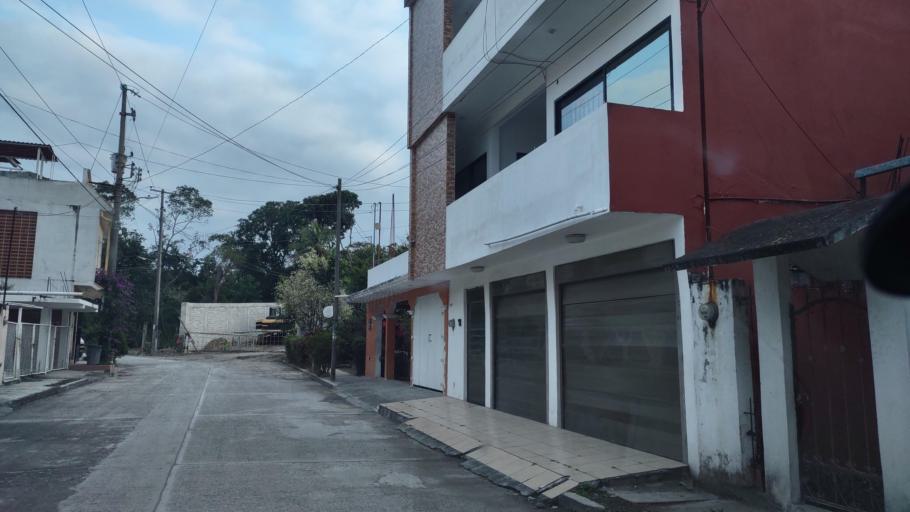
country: MX
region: Veracruz
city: Papantla de Olarte
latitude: 20.4548
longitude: -97.3069
